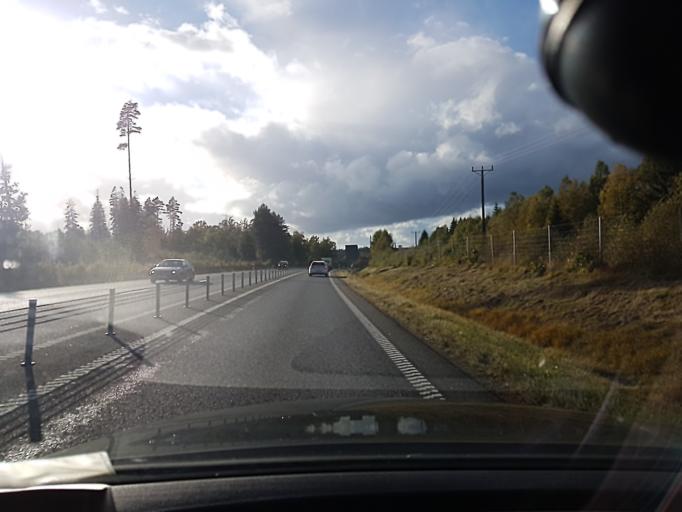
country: SE
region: Kronoberg
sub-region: Ljungby Kommun
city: Ljungby
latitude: 56.8494
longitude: 13.9838
